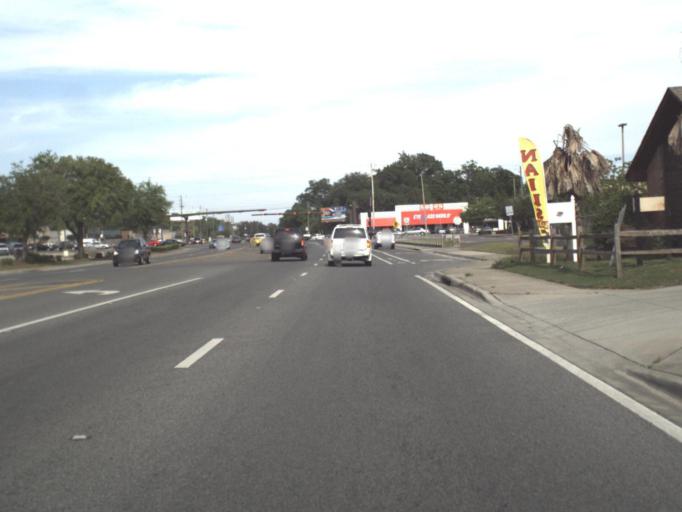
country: US
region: Florida
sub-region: Escambia County
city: Ferry Pass
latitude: 30.4960
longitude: -87.2240
